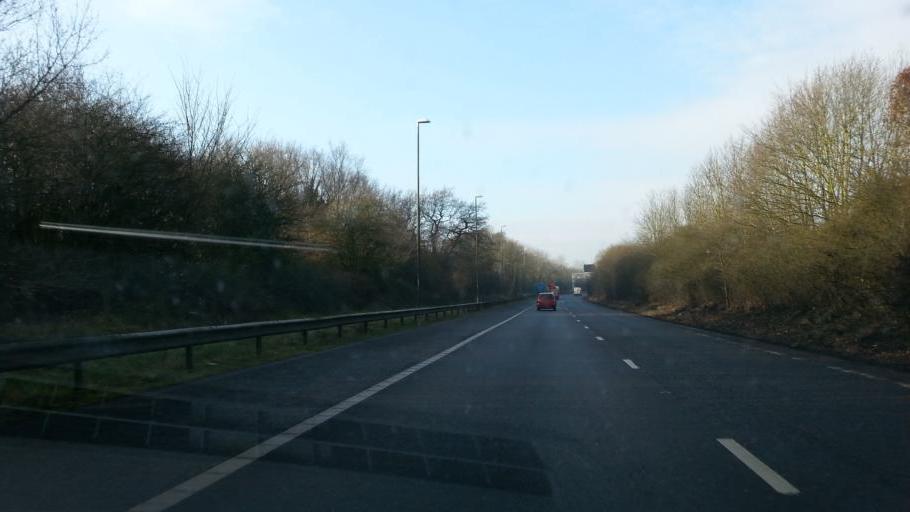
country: GB
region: England
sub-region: Warwickshire
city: Water Orton
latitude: 52.5073
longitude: -1.7362
